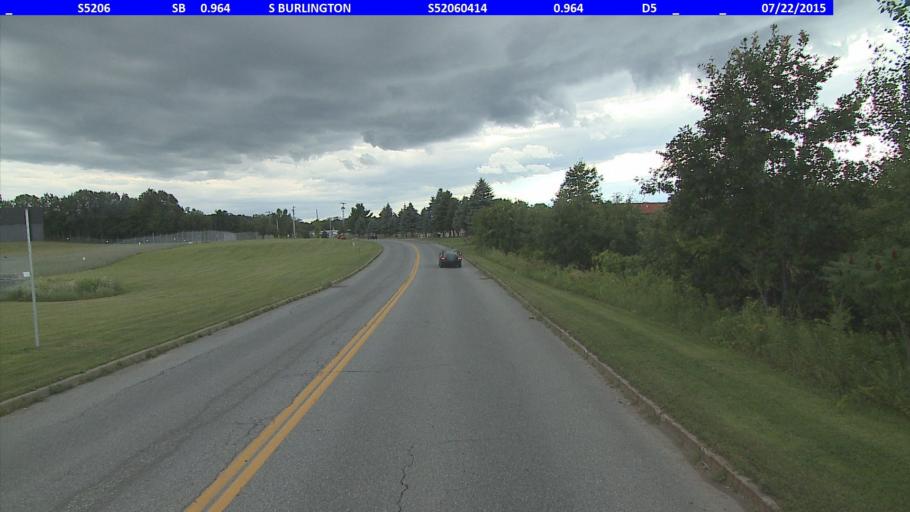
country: US
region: Vermont
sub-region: Chittenden County
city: South Burlington
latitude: 44.4824
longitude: -73.1693
